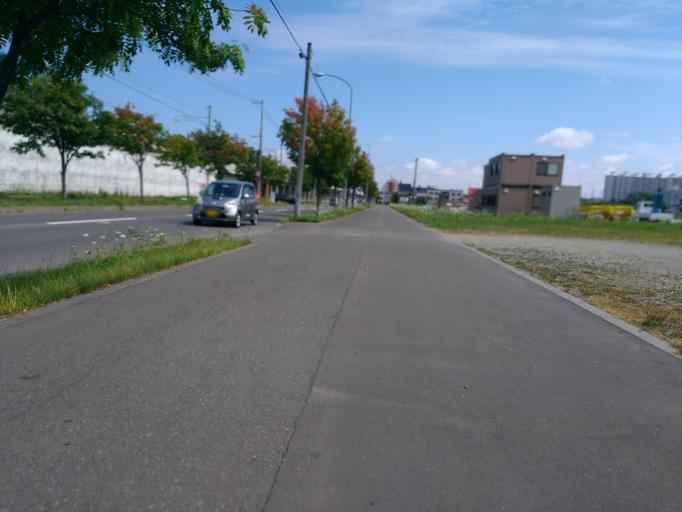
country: JP
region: Hokkaido
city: Ebetsu
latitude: 43.0870
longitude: 141.5226
